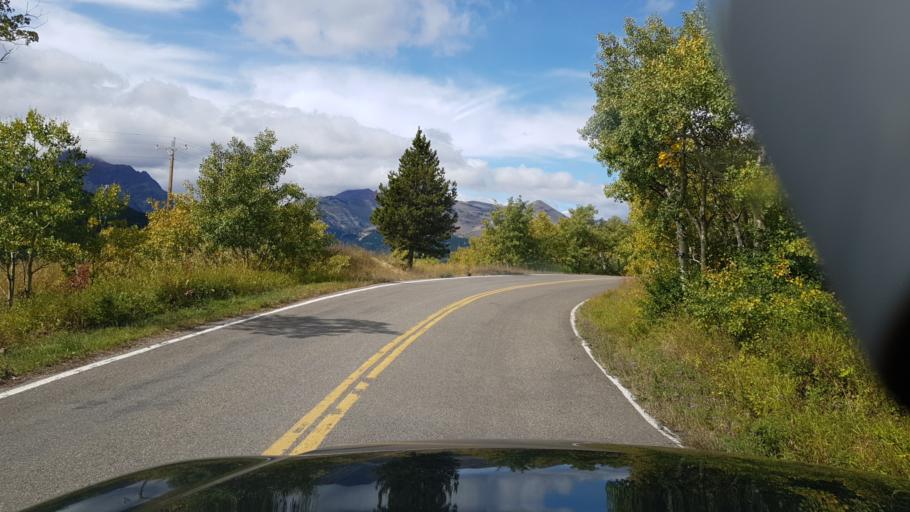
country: US
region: Montana
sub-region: Glacier County
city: South Browning
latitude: 48.4919
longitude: -113.2598
